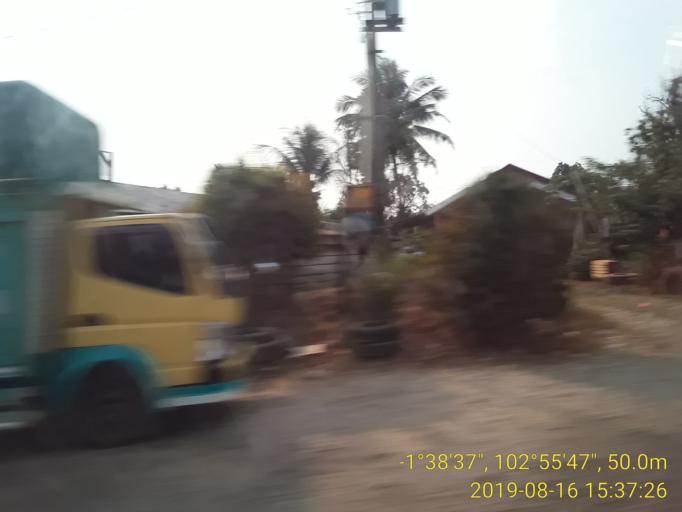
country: ID
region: Jambi
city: Mersam
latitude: -1.6437
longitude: 102.9298
